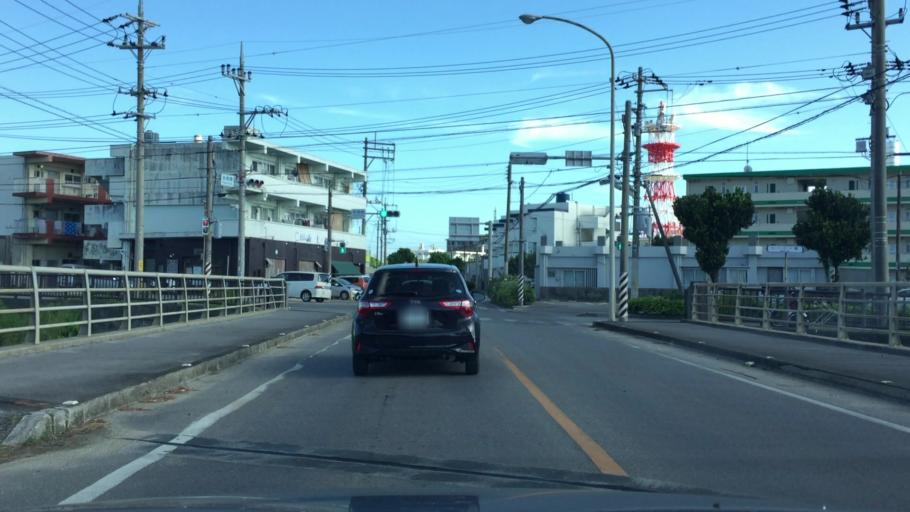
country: JP
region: Okinawa
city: Ishigaki
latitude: 24.3518
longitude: 124.1582
